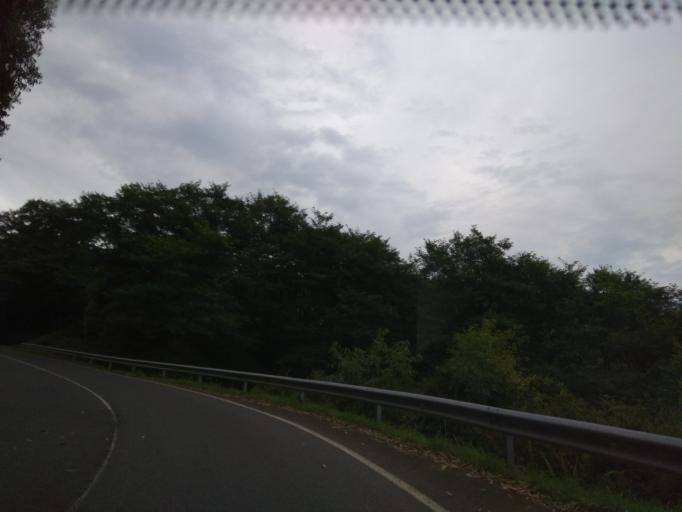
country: ES
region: Cantabria
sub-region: Provincia de Cantabria
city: Hazas de Cesto
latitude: 43.4046
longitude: -3.6002
